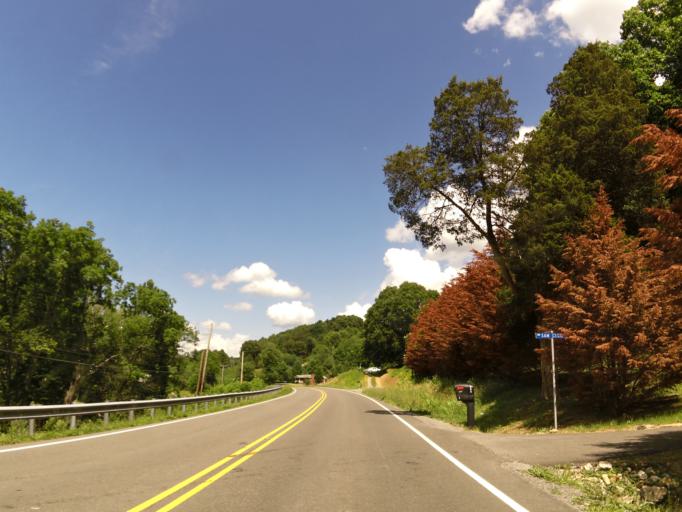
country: US
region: Virginia
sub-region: Lee County
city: Jonesville
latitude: 36.6902
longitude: -83.0948
